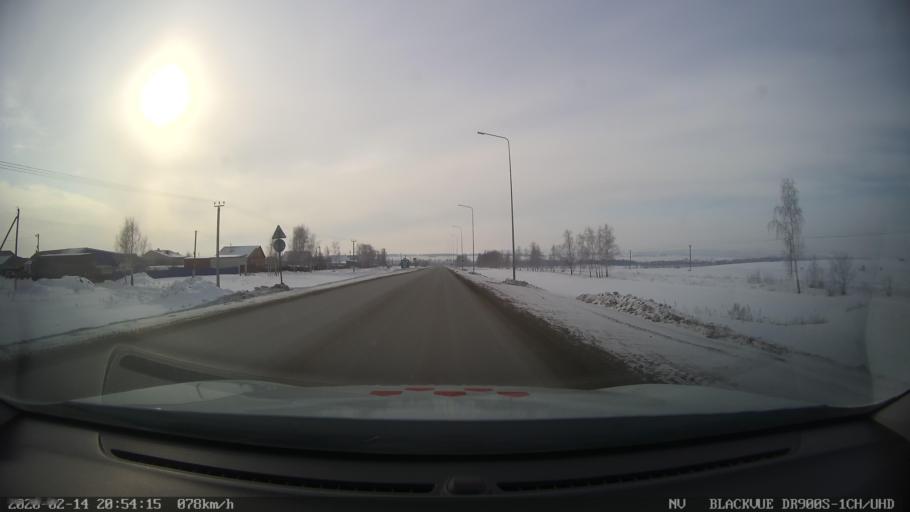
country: RU
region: Tatarstan
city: Kuybyshevskiy Zaton
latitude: 55.1877
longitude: 49.2443
